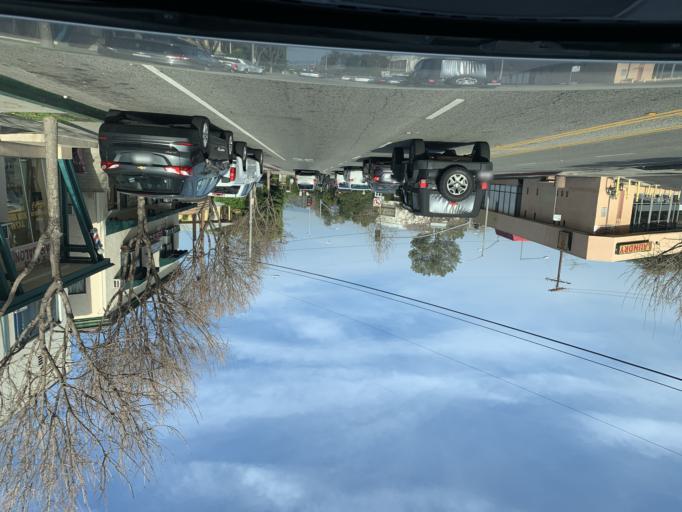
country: US
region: California
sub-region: Los Angeles County
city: Glendale
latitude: 34.1343
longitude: -118.2404
